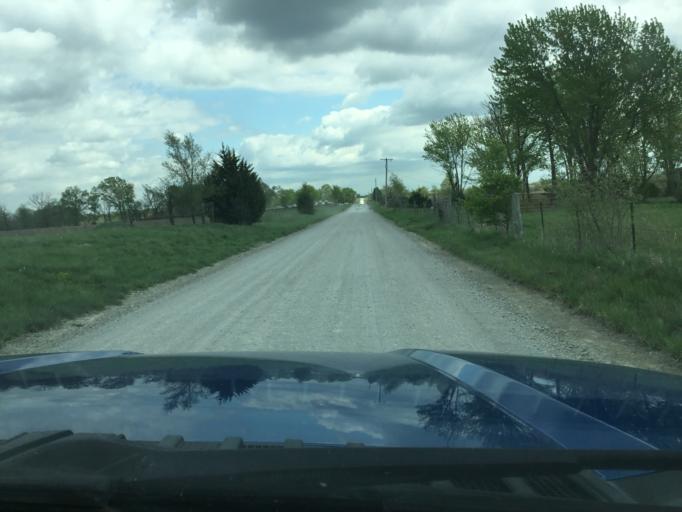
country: US
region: Kansas
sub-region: Douglas County
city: Eudora
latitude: 38.9278
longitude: -95.0893
